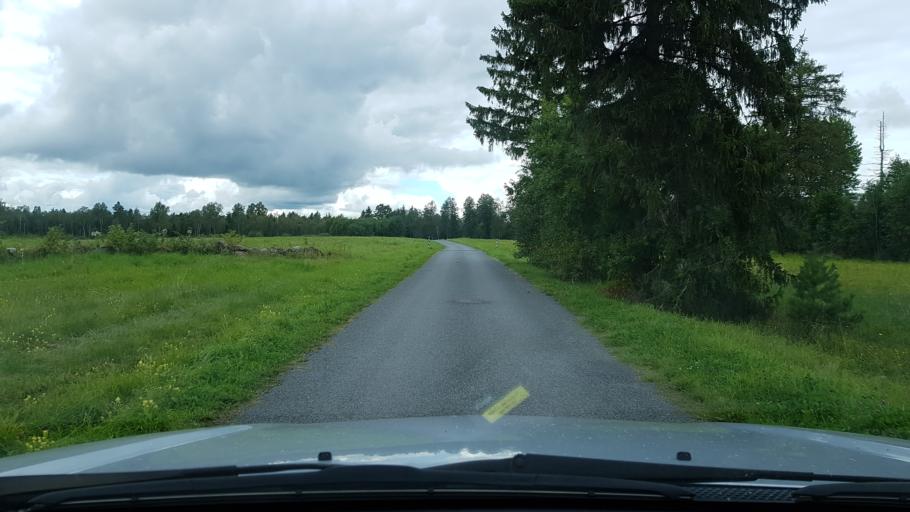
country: EE
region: Harju
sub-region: Rae vald
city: Vaida
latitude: 59.3018
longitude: 25.0358
